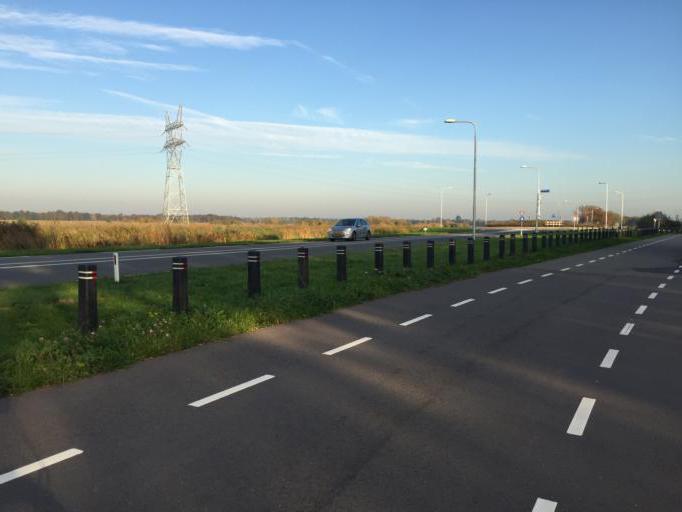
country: NL
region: North Holland
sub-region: Gemeente Wijdemeren
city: Kortenhoef
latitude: 52.2760
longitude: 5.1067
